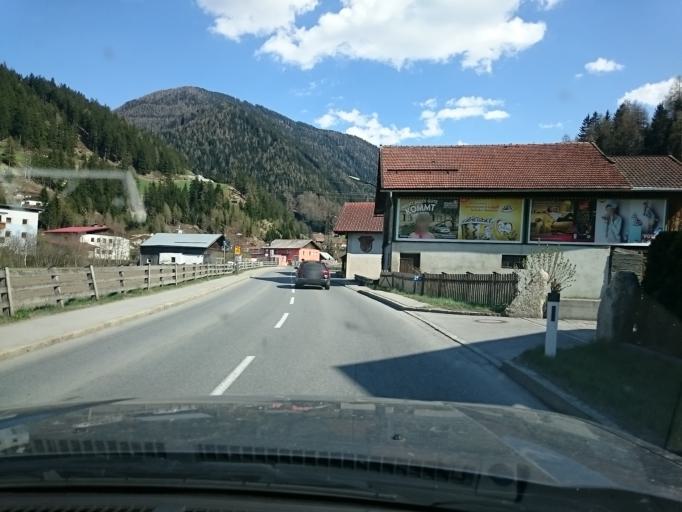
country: AT
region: Tyrol
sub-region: Politischer Bezirk Innsbruck Land
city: Steinach am Brenner
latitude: 47.0850
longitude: 11.4699
